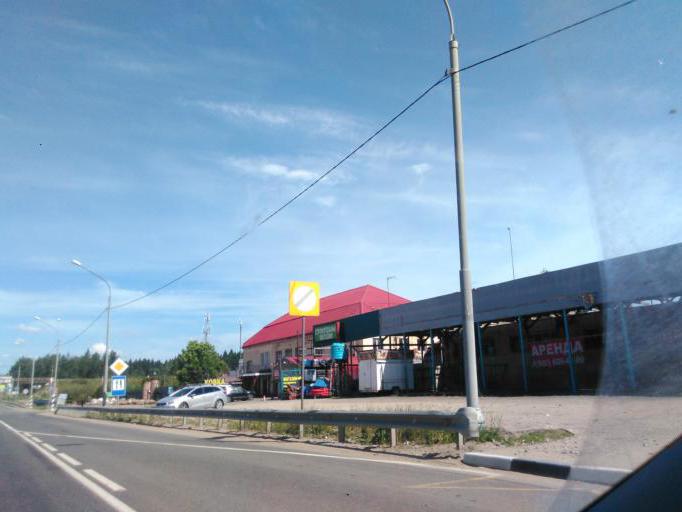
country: RU
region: Moskovskaya
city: Radumlya
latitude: 56.0691
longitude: 37.1350
